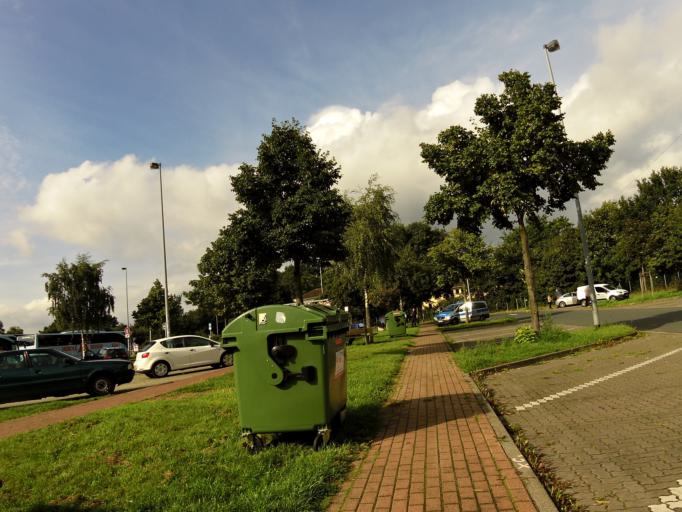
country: DE
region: Lower Saxony
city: Garbsen
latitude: 52.4223
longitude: 9.5552
